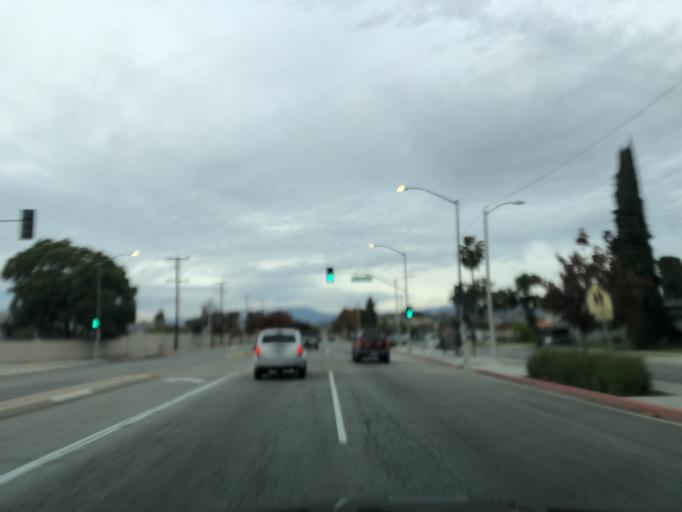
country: US
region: California
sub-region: Los Angeles County
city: South Whittier
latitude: 33.9437
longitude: -118.0465
